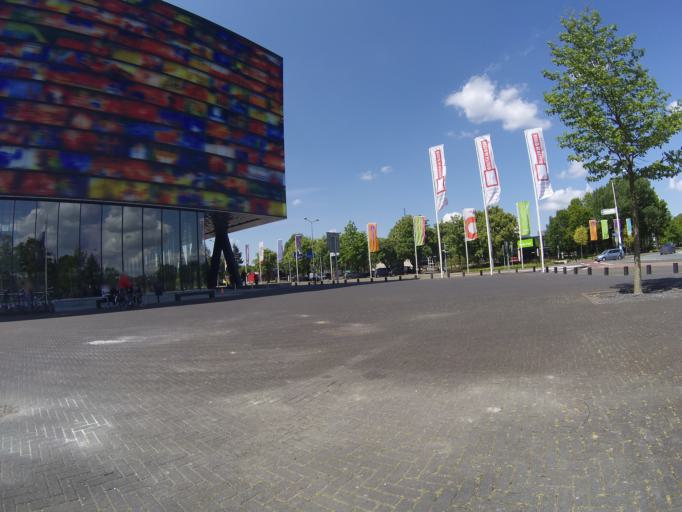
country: NL
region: North Holland
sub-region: Gemeente Hilversum
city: Hilversum
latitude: 52.2354
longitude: 5.1733
